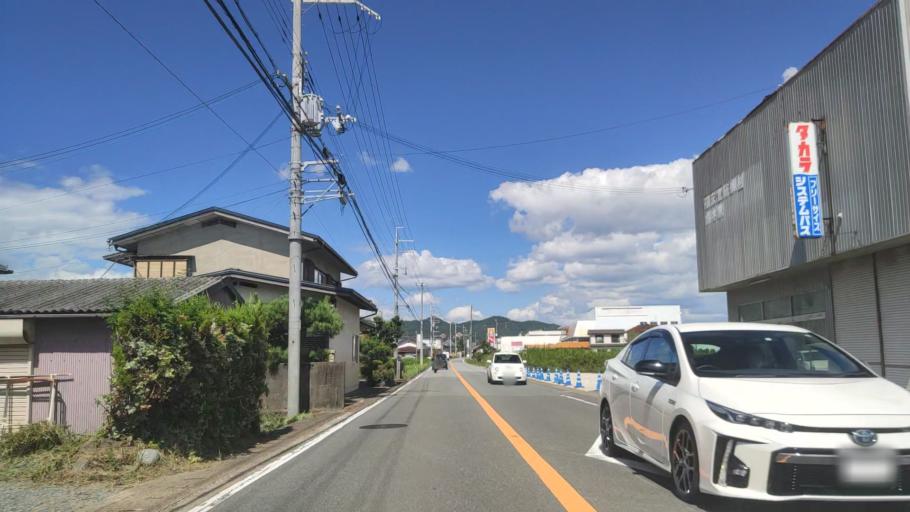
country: JP
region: Kyoto
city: Fukuchiyama
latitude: 35.2207
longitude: 135.1304
